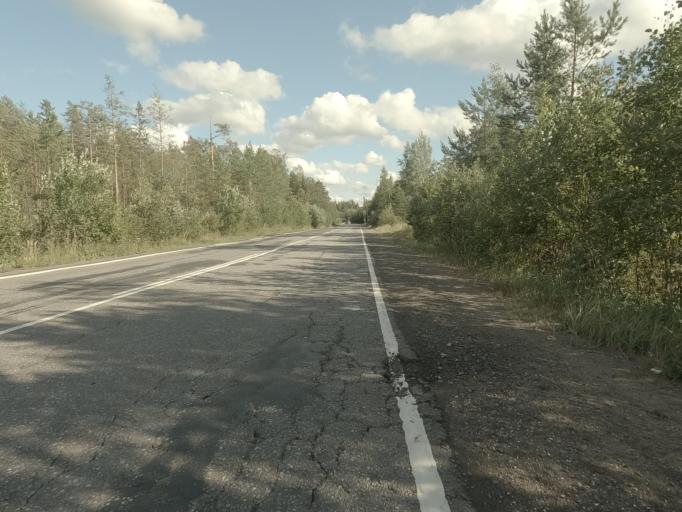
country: RU
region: Leningrad
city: Borisova Griva
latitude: 59.9883
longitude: 30.8866
